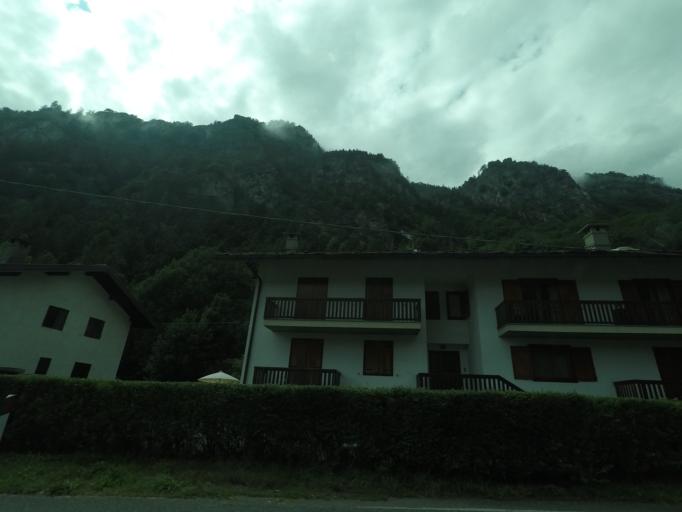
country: IT
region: Aosta Valley
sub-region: Valle d'Aosta
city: Antey-Saint-Andre
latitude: 45.8102
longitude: 7.5878
